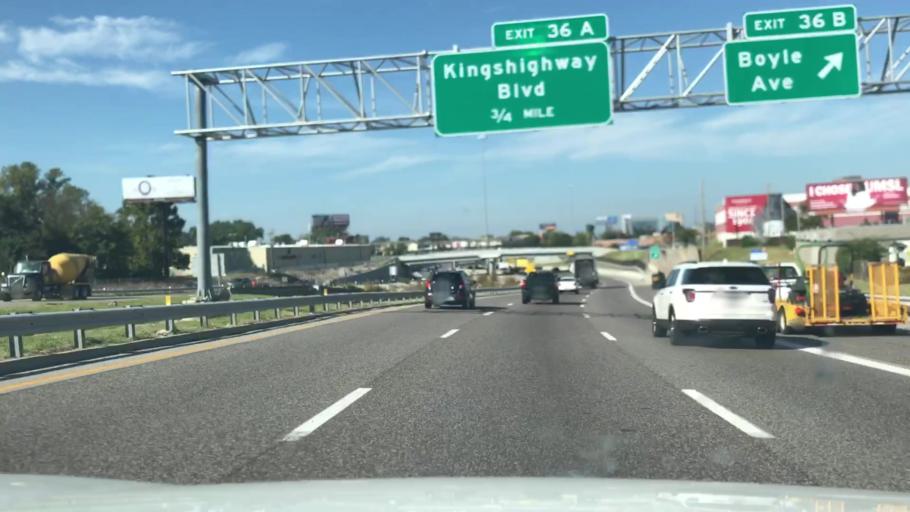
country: US
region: Missouri
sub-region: City of Saint Louis
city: St. Louis
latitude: 38.6312
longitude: -90.2503
